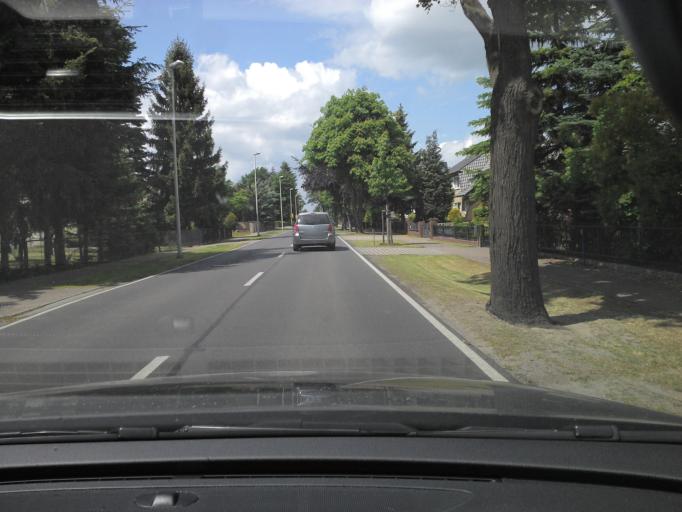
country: DE
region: Brandenburg
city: Werben
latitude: 51.8104
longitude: 14.1988
